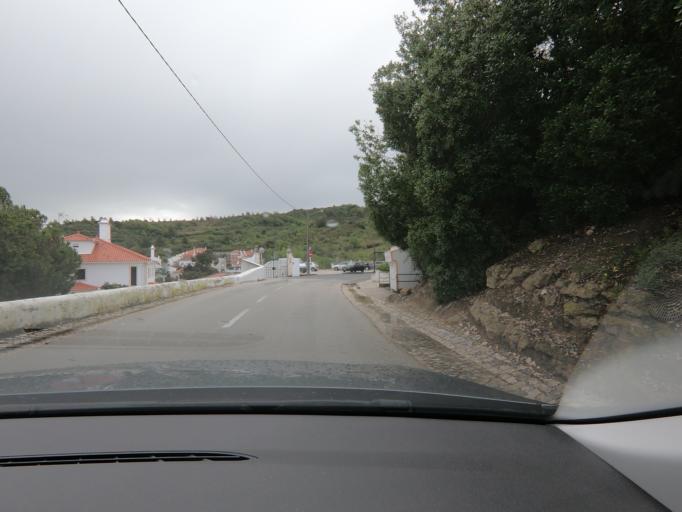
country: PT
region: Lisbon
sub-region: Alenquer
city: Alenquer
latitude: 39.0528
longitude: -9.0101
